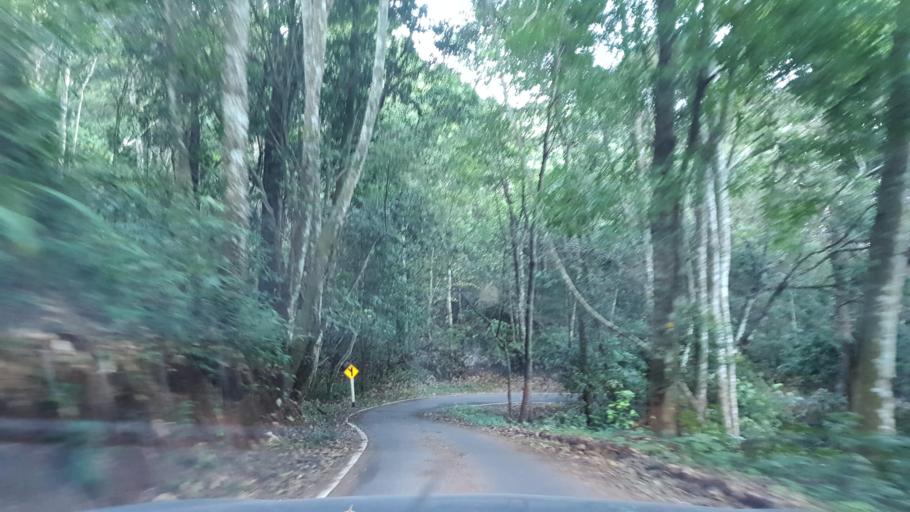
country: TH
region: Chiang Mai
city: Chiang Mai
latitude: 18.8253
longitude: 98.8927
